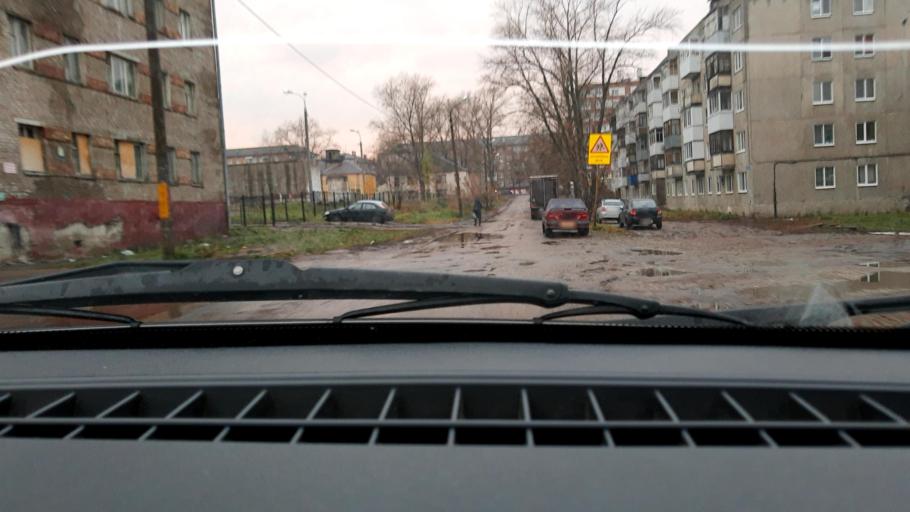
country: RU
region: Bashkortostan
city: Ufa
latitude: 54.8174
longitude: 56.1172
